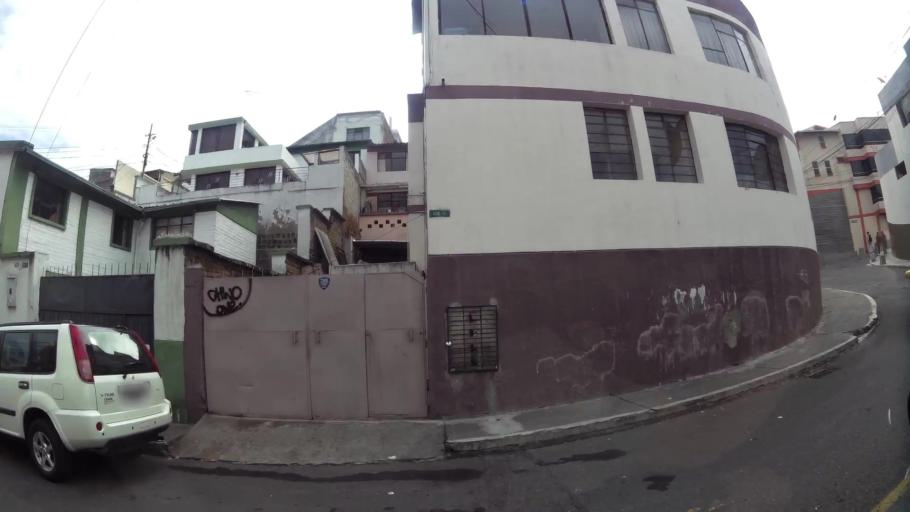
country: EC
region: Pichincha
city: Quito
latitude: -0.2170
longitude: -78.4869
